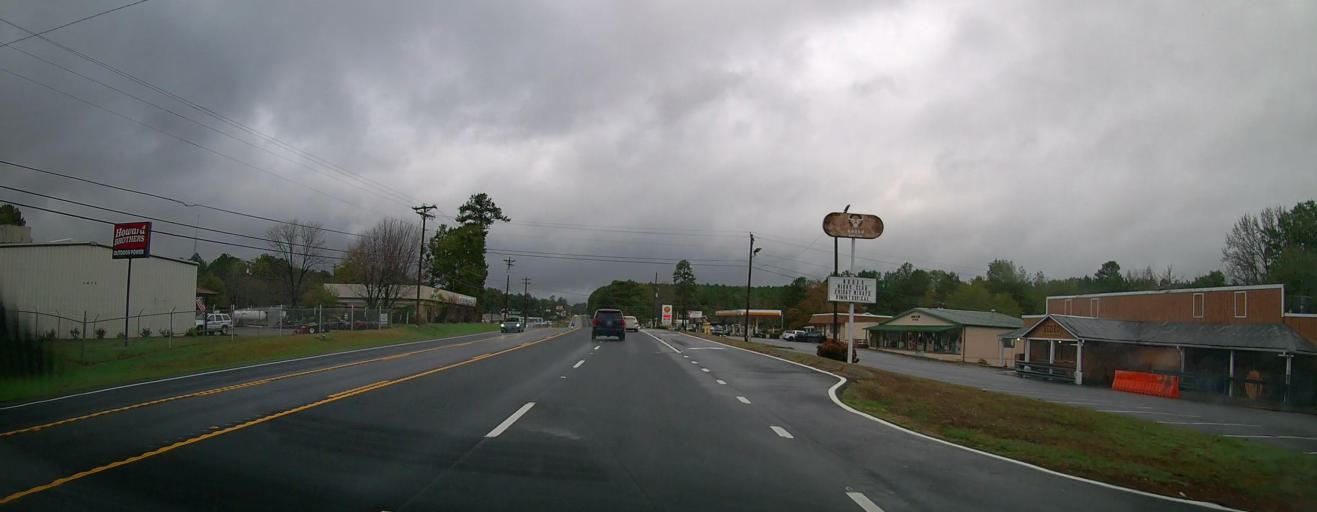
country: US
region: Georgia
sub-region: Clarke County
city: Country Club Estates
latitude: 33.9929
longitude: -83.3792
